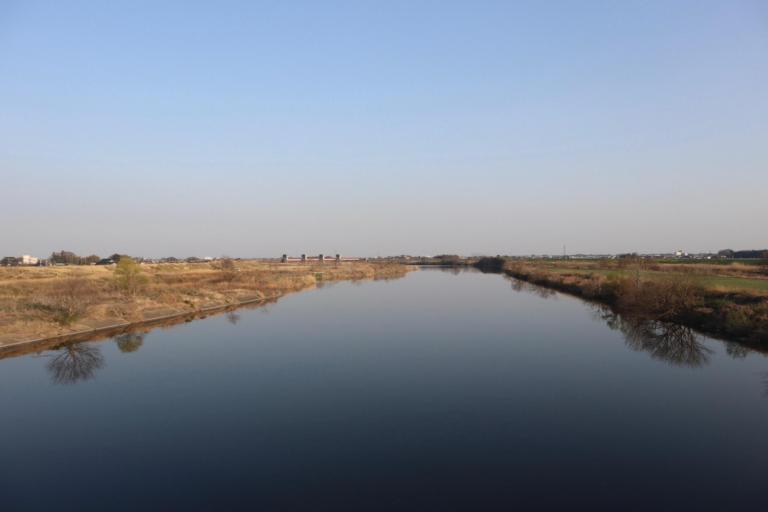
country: JP
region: Gunma
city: Tatebayashi
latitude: 36.2720
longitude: 139.5558
